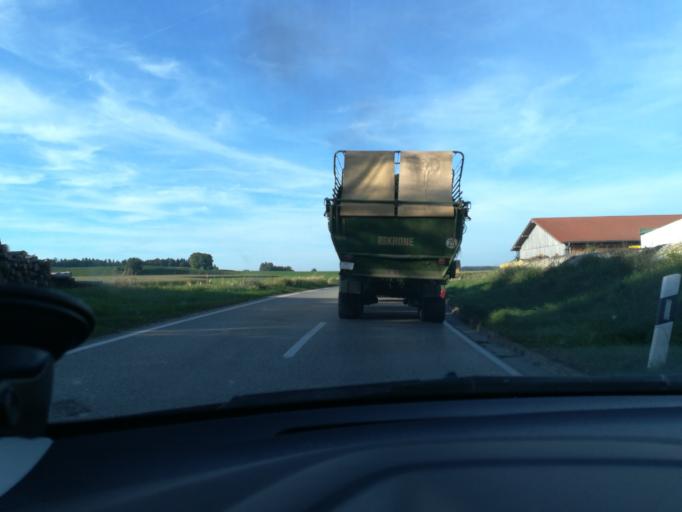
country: DE
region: Bavaria
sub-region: Upper Bavaria
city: Glonn
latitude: 47.9601
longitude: 11.8615
